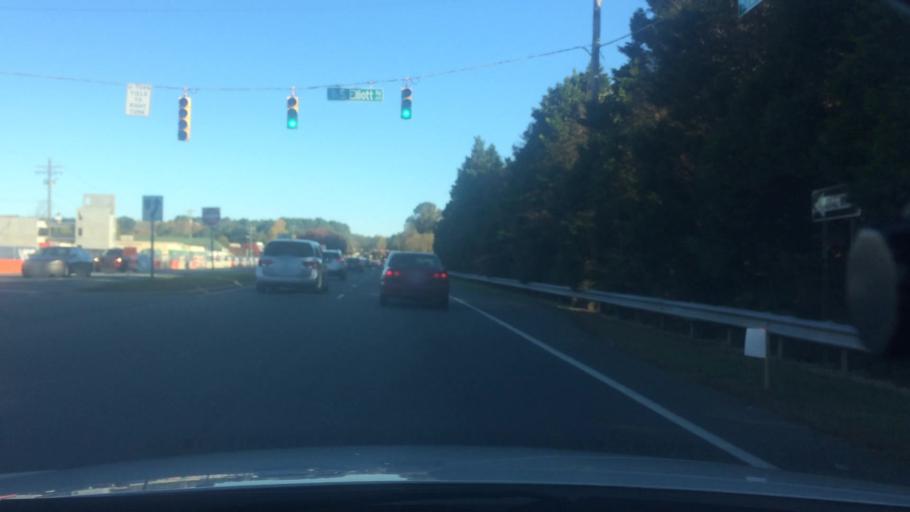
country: US
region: North Carolina
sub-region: Orange County
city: Chapel Hill
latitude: 35.9324
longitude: -79.0239
